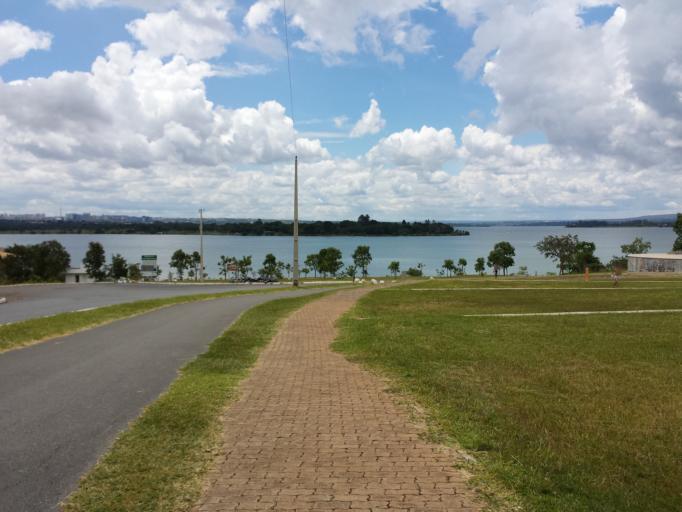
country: BR
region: Federal District
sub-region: Brasilia
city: Brasilia
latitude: -15.7984
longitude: -47.8104
